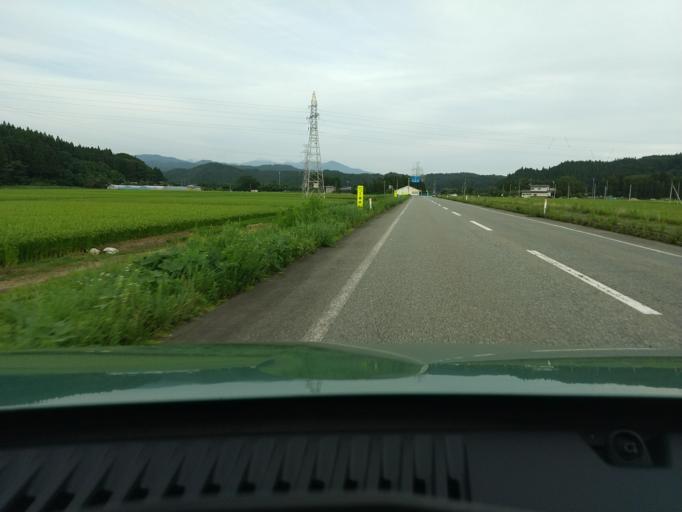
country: JP
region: Akita
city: Akita Shi
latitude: 39.7925
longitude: 140.1084
